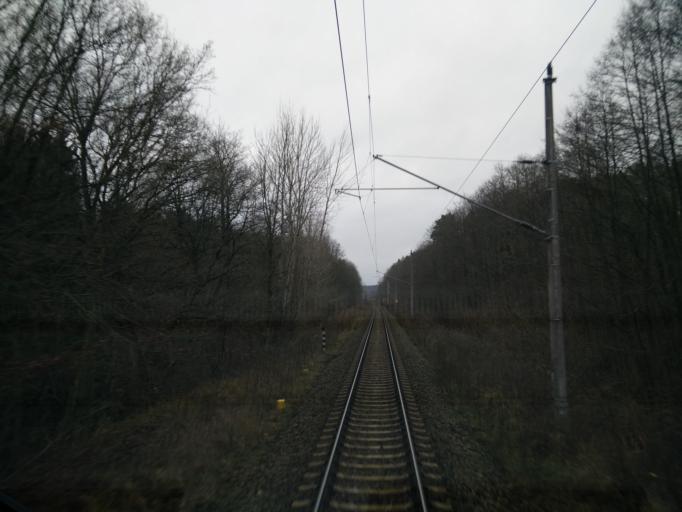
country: DE
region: Mecklenburg-Vorpommern
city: Bad Kleinen
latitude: 53.7999
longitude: 11.4842
